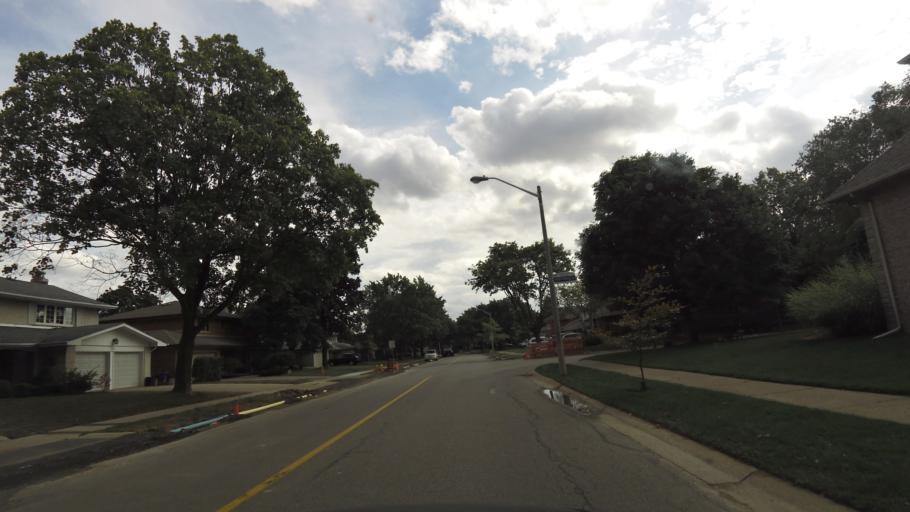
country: CA
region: Ontario
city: Etobicoke
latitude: 43.6328
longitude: -79.5829
